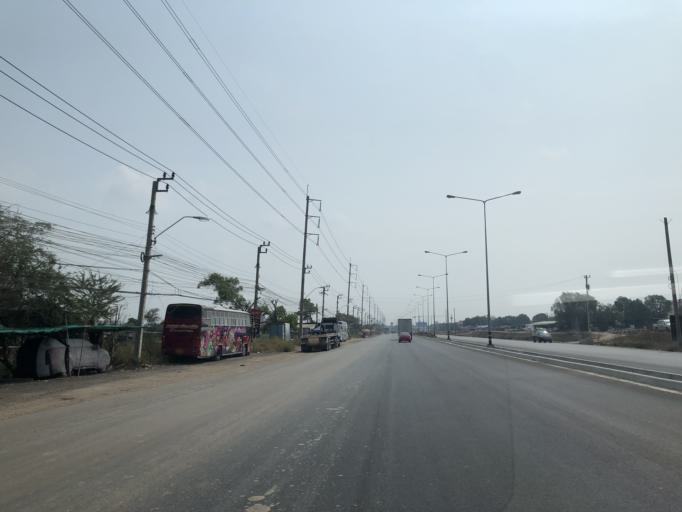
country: TH
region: Samut Prakan
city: Bang Bo
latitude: 13.5114
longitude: 100.7968
